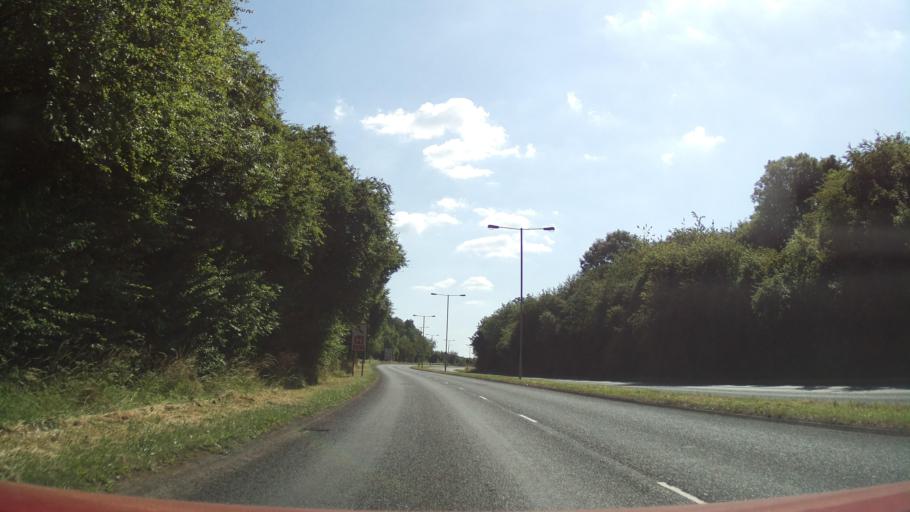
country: GB
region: England
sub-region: Worcestershire
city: Redditch
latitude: 52.2945
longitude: -1.9270
